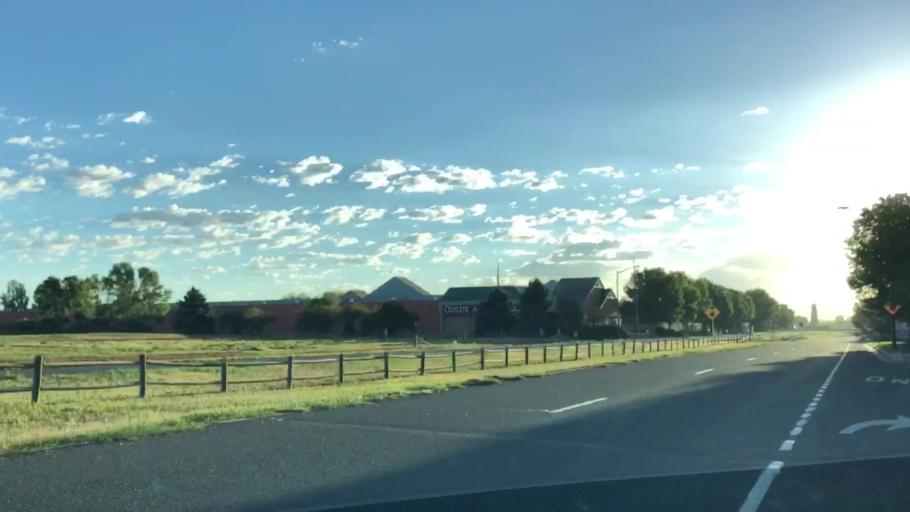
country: US
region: Colorado
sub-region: Larimer County
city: Loveland
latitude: 40.4106
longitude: -104.9987
